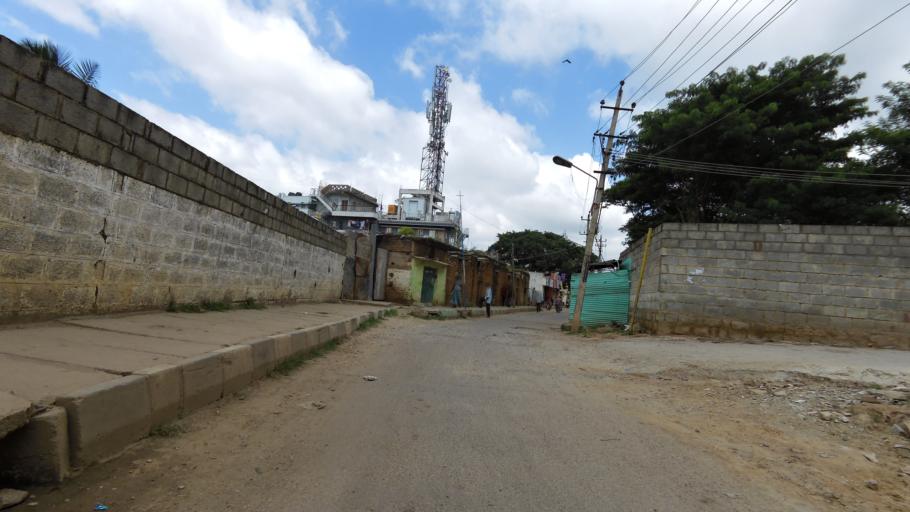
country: IN
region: Karnataka
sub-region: Bangalore Urban
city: Bangalore
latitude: 12.9931
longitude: 77.6237
